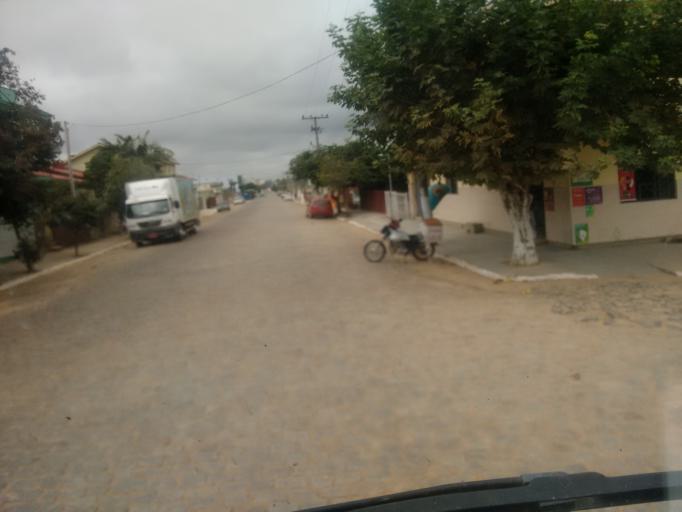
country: BR
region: Rio Grande do Sul
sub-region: Camaqua
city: Camaqua
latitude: -30.8404
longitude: -51.8152
